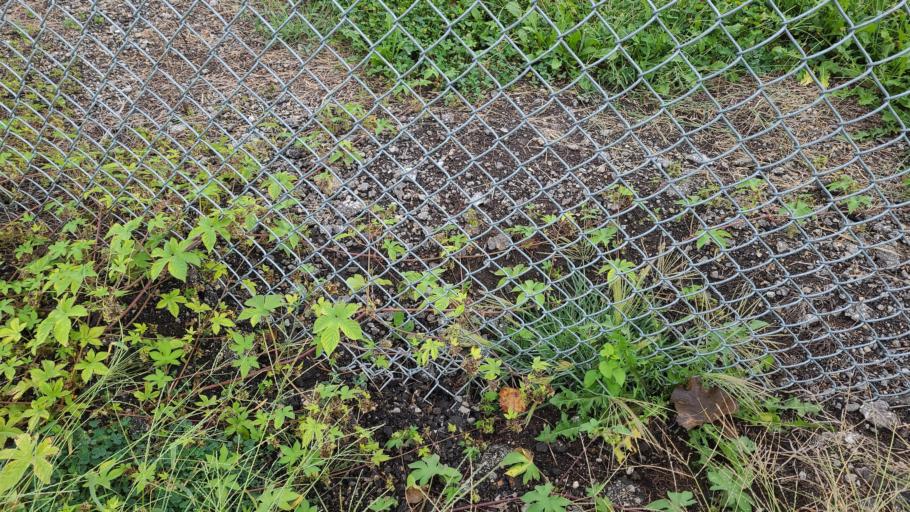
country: US
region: Kansas
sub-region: Douglas County
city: Lawrence
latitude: 39.0103
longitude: -95.2185
